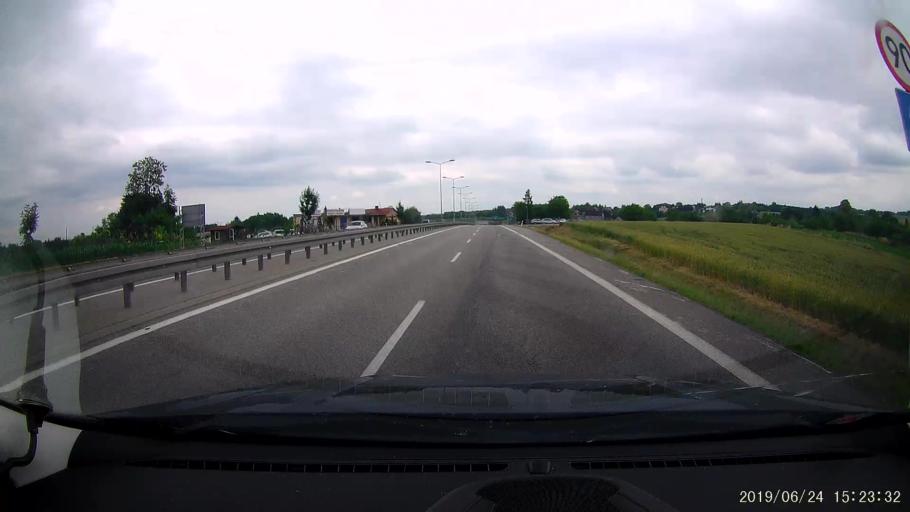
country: PL
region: Subcarpathian Voivodeship
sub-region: Powiat jaroslawski
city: Wierzbna
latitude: 50.0265
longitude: 22.6284
